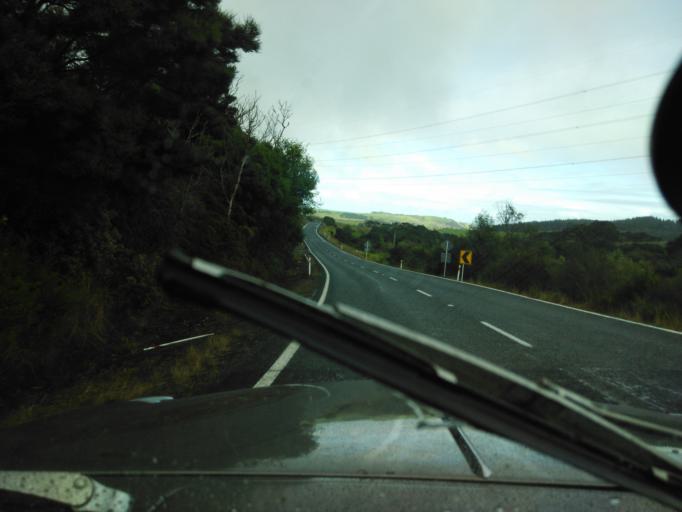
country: NZ
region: Auckland
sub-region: Auckland
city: Parakai
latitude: -36.4754
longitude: 174.4478
